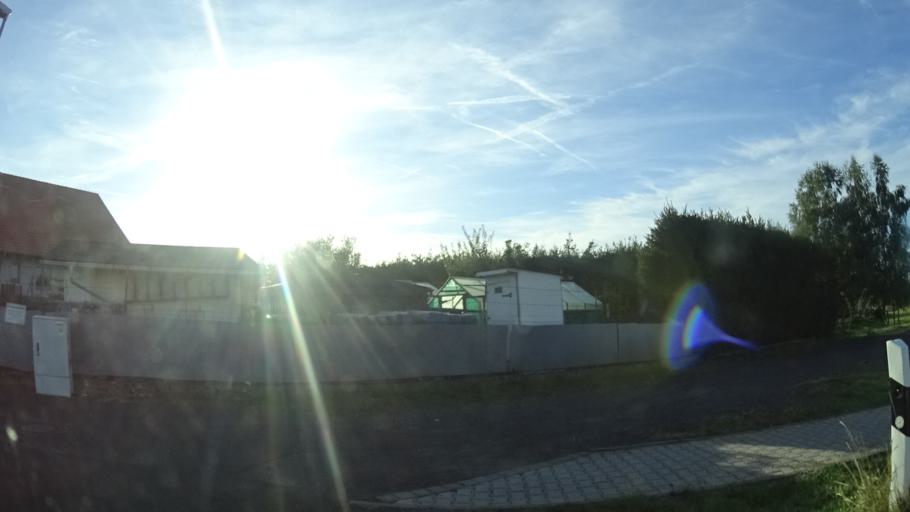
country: DE
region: Hesse
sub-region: Regierungsbezirk Darmstadt
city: Wachtersbach
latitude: 50.2884
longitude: 9.2615
